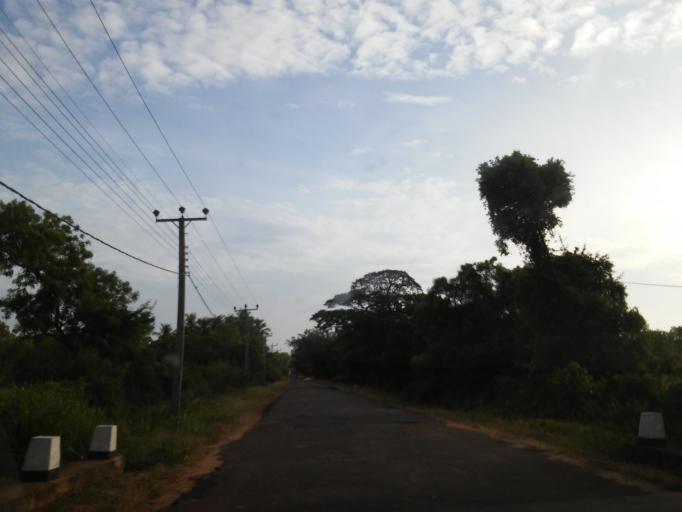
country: LK
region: Central
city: Sigiriya
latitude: 8.1299
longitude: 80.6333
